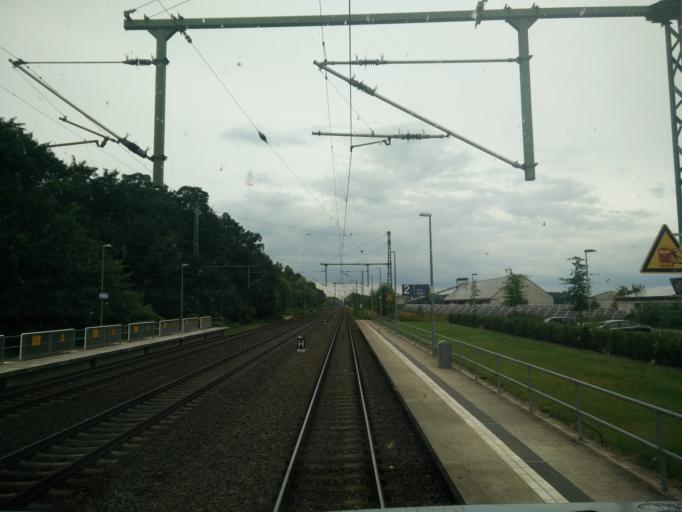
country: DE
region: Brandenburg
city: Friesack
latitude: 52.7609
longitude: 12.5875
